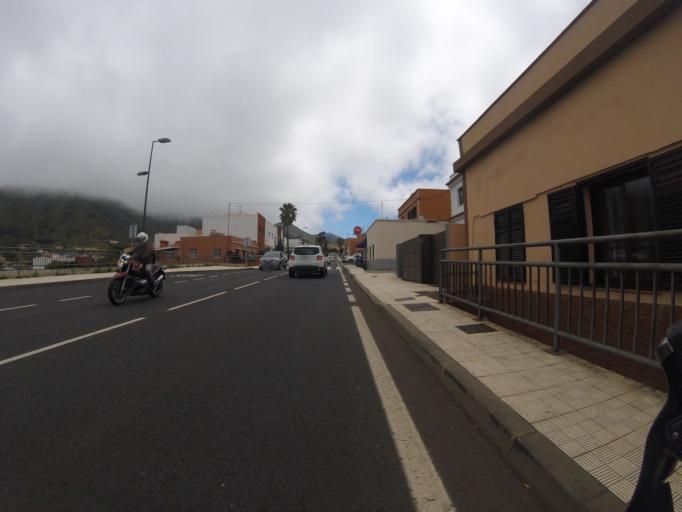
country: ES
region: Canary Islands
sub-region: Provincia de Santa Cruz de Tenerife
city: Tegueste
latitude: 28.5225
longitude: -16.3433
